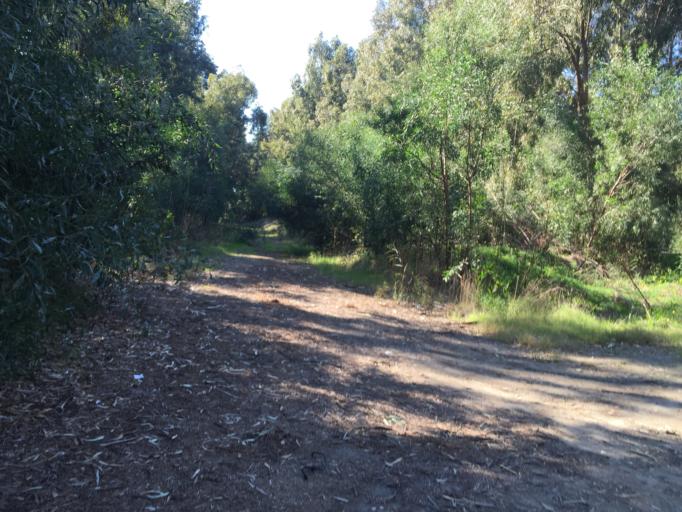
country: CY
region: Larnaka
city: Kolossi
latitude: 34.6272
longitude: 32.9480
